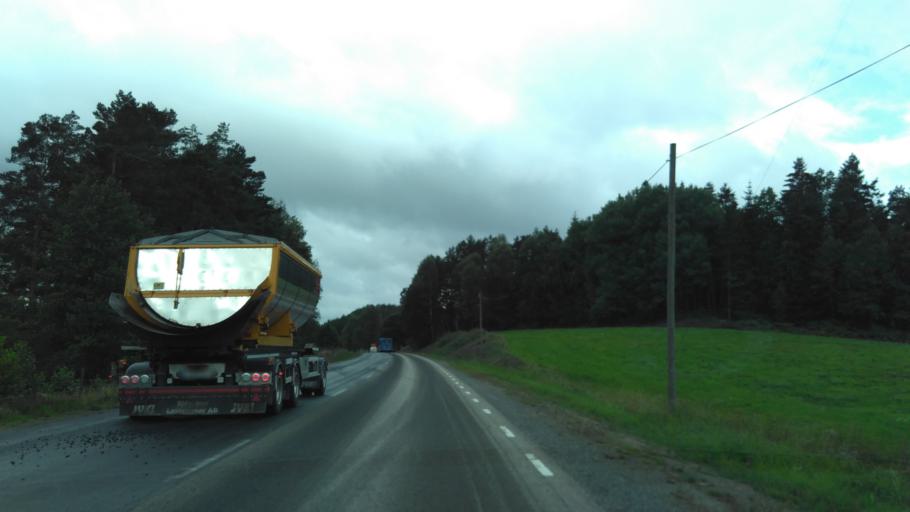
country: SE
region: Vaestra Goetaland
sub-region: Marks Kommun
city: Fritsla
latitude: 57.5676
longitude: 12.8199
